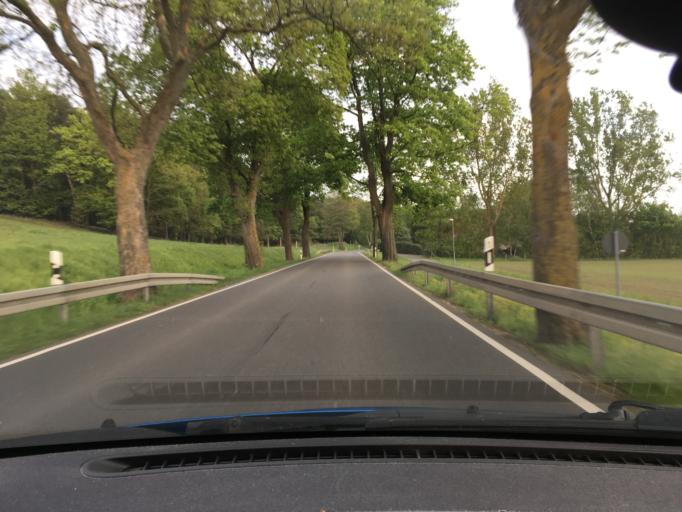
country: DE
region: Mecklenburg-Vorpommern
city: Boizenburg
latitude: 53.4068
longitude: 10.7449
